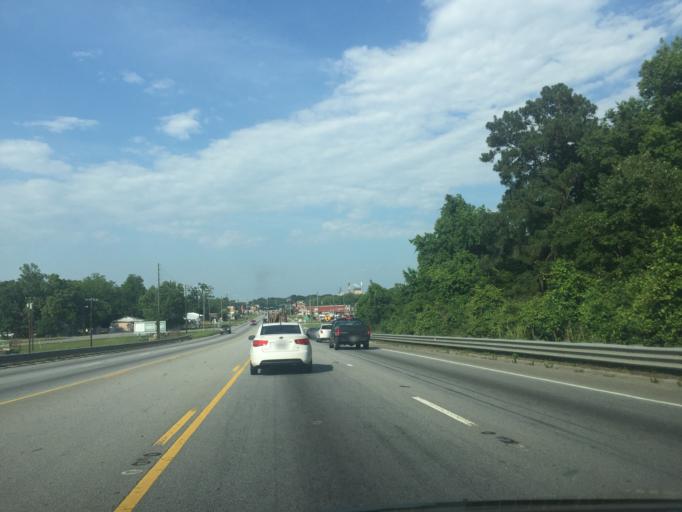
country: US
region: Georgia
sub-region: Chatham County
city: Garden City
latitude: 32.0918
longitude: -81.1512
